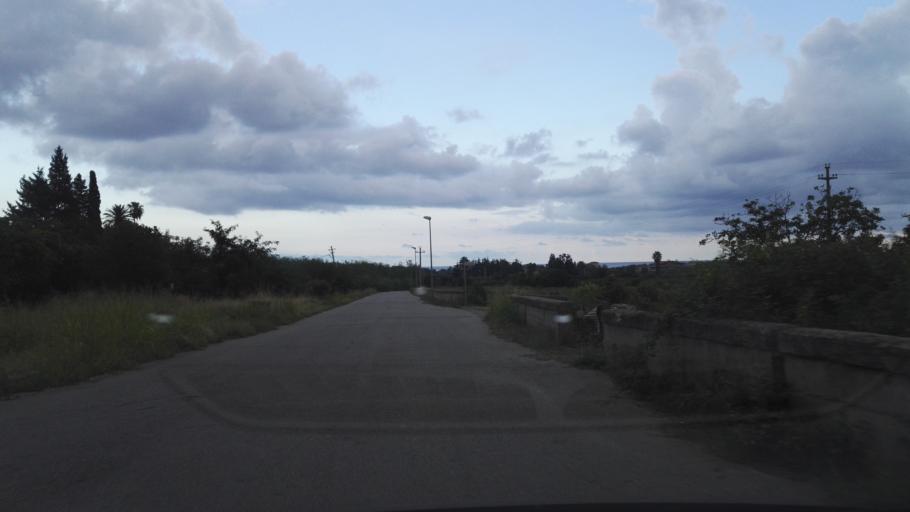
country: IT
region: Calabria
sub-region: Provincia di Reggio Calabria
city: Caulonia Marina
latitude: 38.3615
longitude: 16.4639
